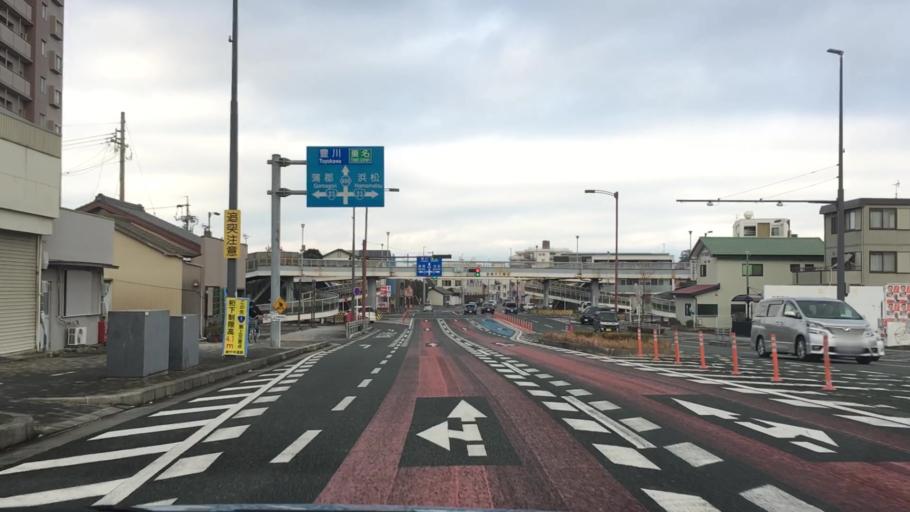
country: JP
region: Aichi
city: Toyohashi
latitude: 34.7686
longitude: 137.3829
